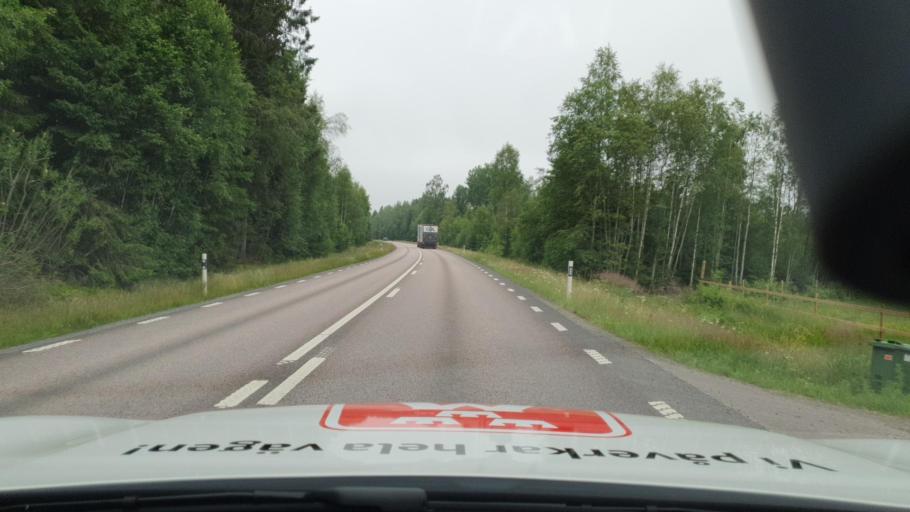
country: SE
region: Vaermland
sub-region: Sunne Kommun
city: Sunne
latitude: 59.7031
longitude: 13.1491
